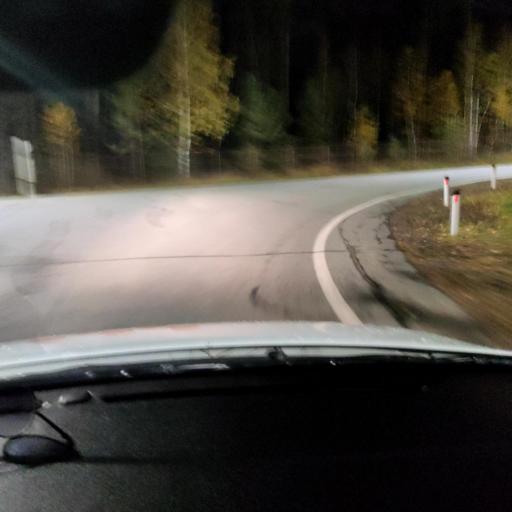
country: RU
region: Tatarstan
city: Verkhniy Uslon
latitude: 55.6398
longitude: 49.0230
